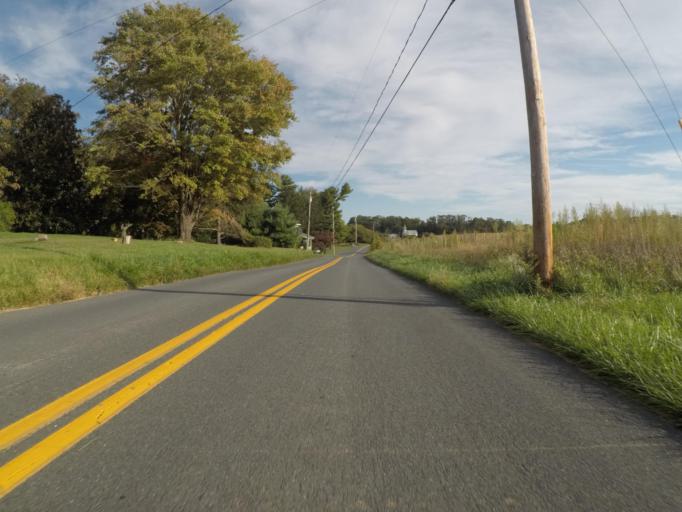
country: US
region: Maryland
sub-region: Carroll County
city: Hampstead
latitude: 39.5486
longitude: -76.8086
